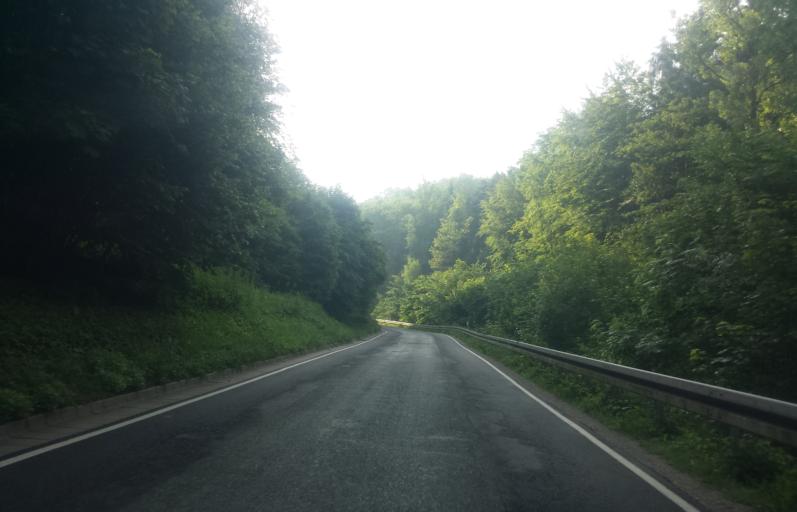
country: DE
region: Bavaria
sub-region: Upper Franconia
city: Ebermannstadt
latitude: 49.7835
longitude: 11.2134
